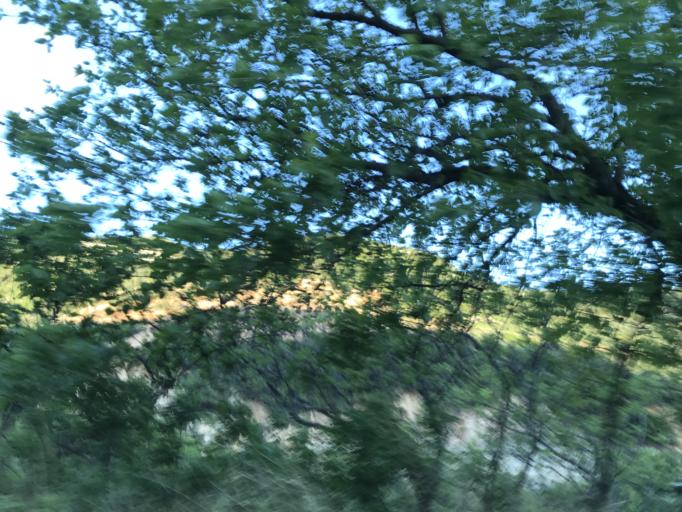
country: TR
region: Hatay
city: Buyukcat
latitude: 36.0847
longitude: 36.0515
